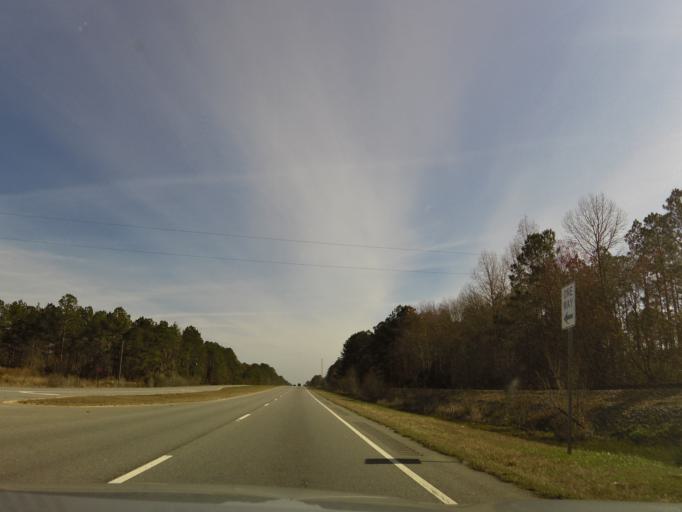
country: US
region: Georgia
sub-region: Lowndes County
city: Valdosta
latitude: 30.8624
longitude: -83.1957
